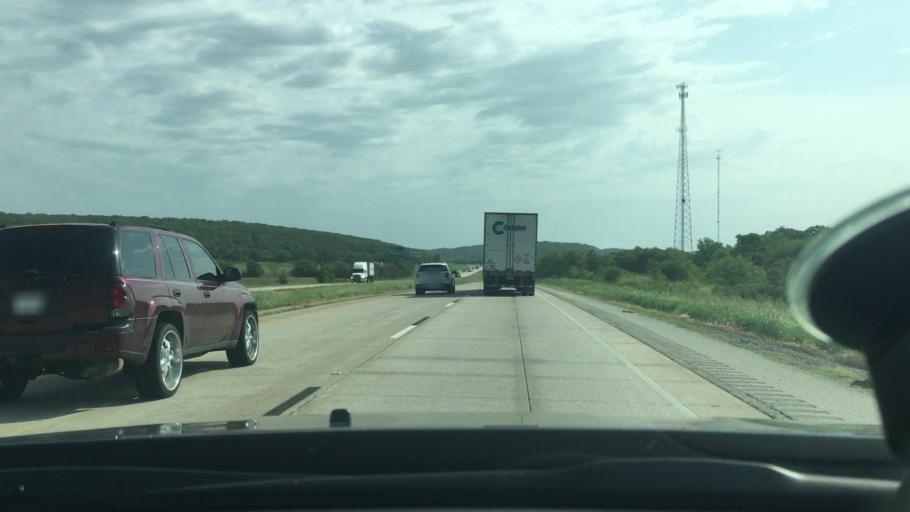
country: US
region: Oklahoma
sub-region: Atoka County
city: Atoka
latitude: 34.4278
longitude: -96.0868
